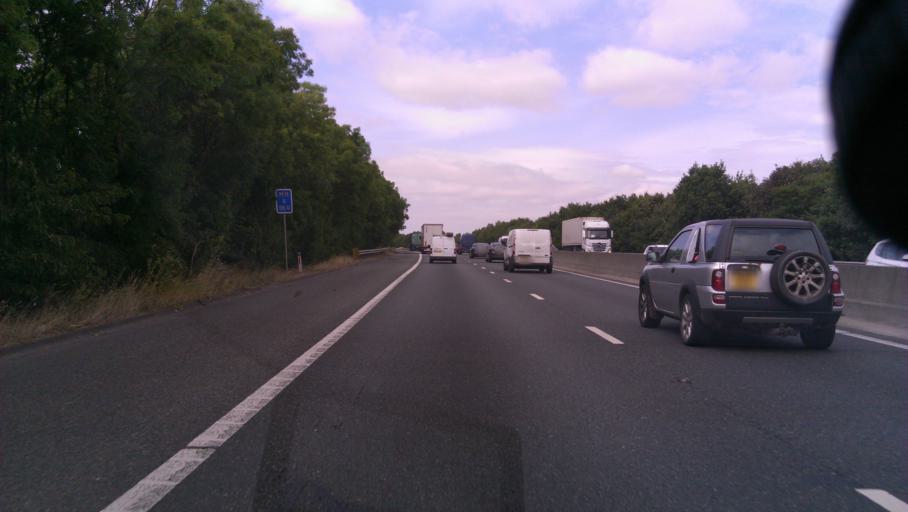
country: GB
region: England
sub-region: Essex
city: Elsenham
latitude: 51.9491
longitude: 0.2159
